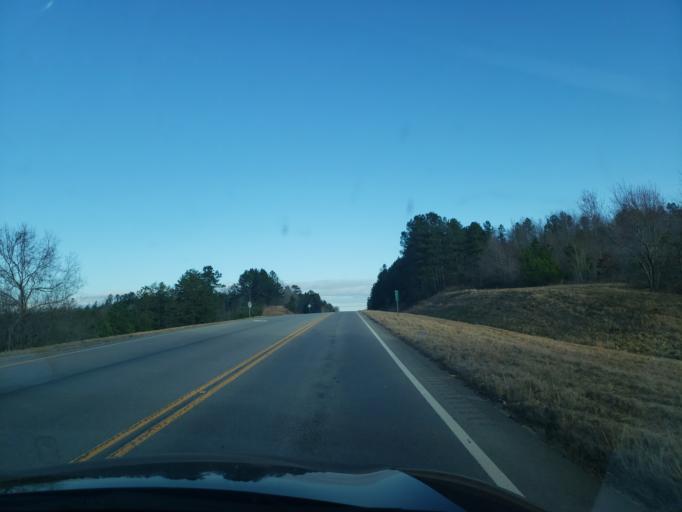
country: US
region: Alabama
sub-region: Cleburne County
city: Heflin
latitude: 33.4895
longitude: -85.5966
